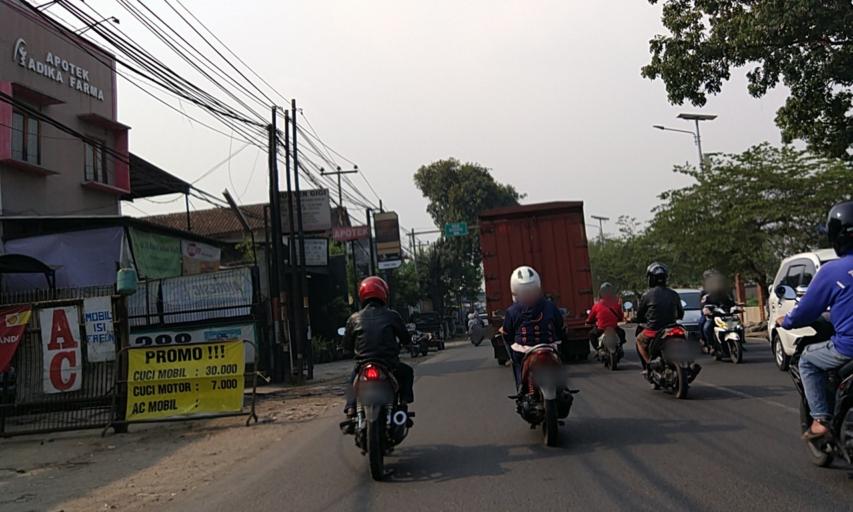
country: ID
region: West Java
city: Margahayukencana
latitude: -6.9773
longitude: 107.5612
